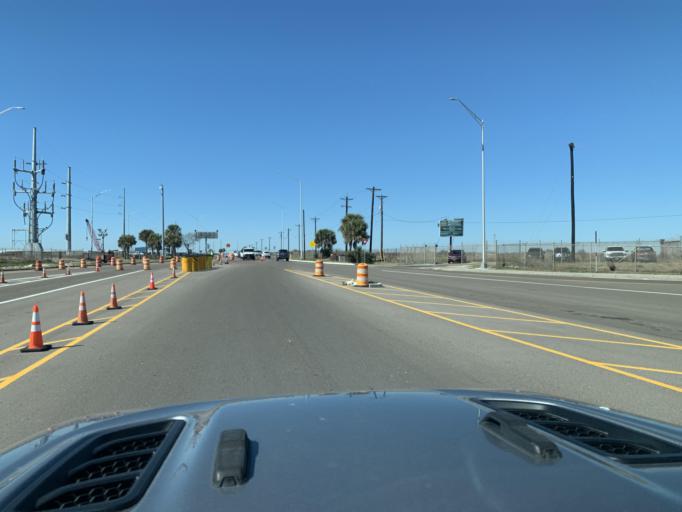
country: US
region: Texas
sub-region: Nueces County
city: Port Aransas
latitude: 27.8445
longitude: -97.0708
